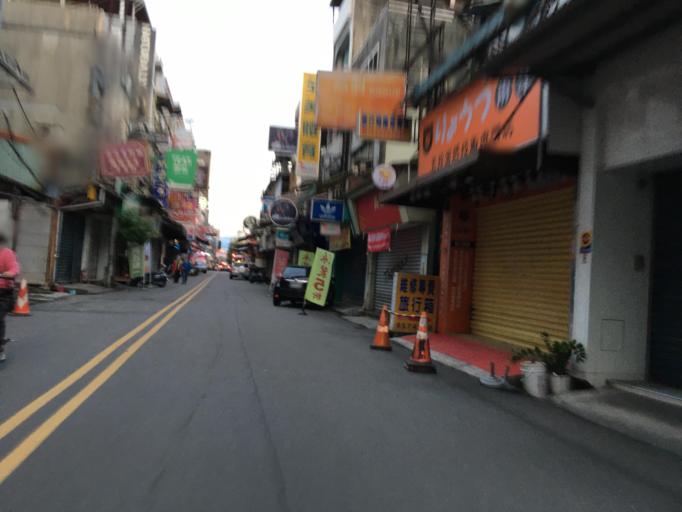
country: TW
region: Taiwan
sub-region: Yilan
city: Yilan
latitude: 24.6754
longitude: 121.7700
